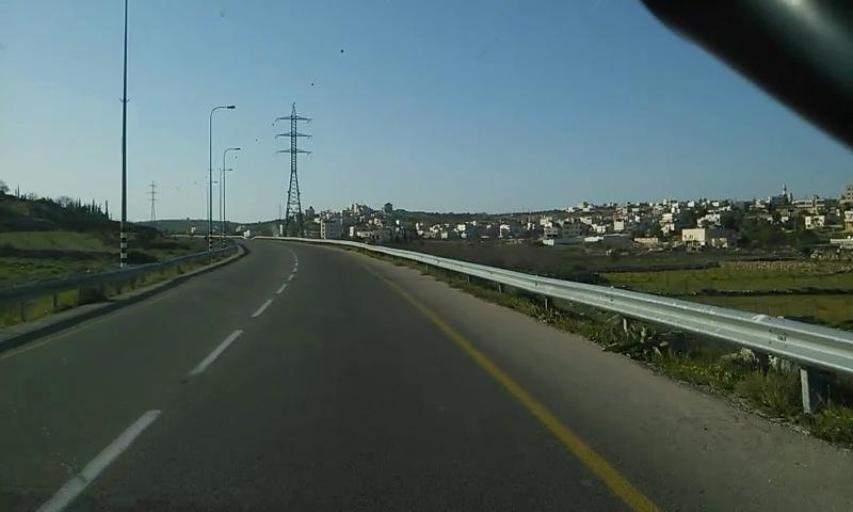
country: PS
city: Bayt `Inun
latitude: 31.5588
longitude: 35.1327
